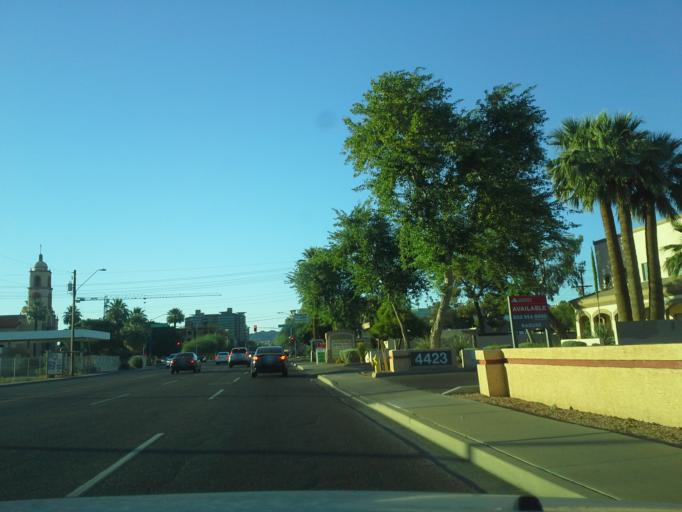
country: US
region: Arizona
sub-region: Maricopa County
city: Phoenix
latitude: 33.5009
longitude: -112.0301
